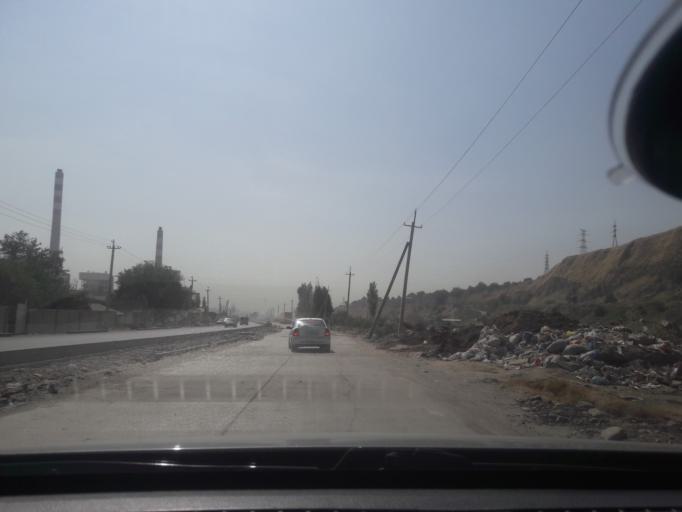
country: TJ
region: Dushanbe
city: Dushanbe
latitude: 38.6171
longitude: 68.7683
